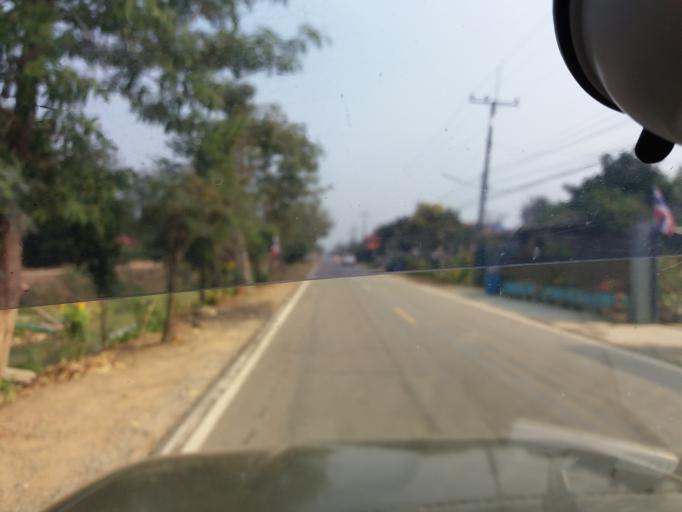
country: TH
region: Suphan Buri
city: Doem Bang Nang Buat
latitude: 14.8906
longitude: 100.1847
